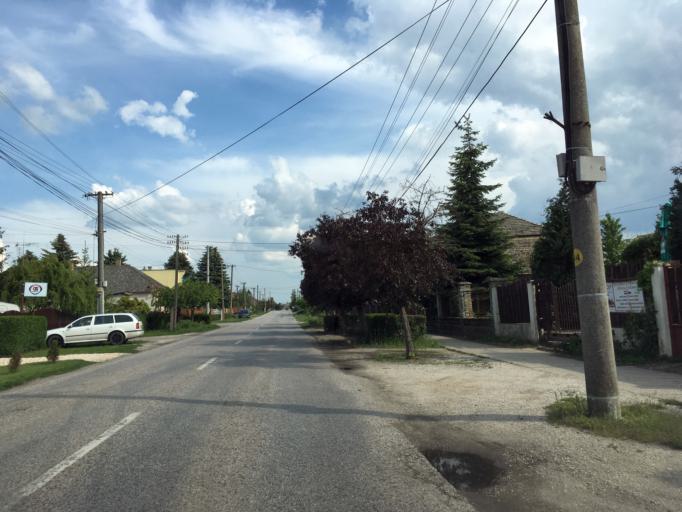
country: SK
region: Nitriansky
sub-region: Okres Komarno
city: Hurbanovo
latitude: 47.8052
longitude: 18.2317
